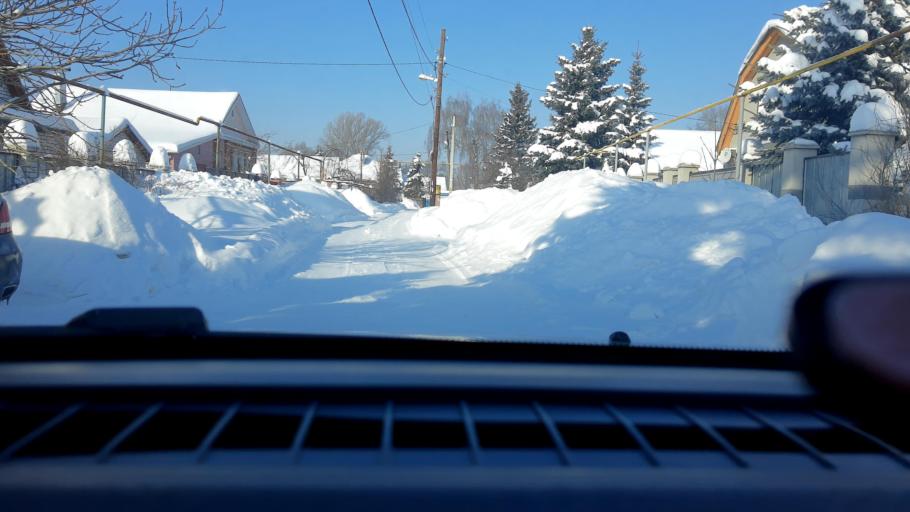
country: RU
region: Nizjnij Novgorod
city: Afonino
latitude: 56.1954
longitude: 44.0529
